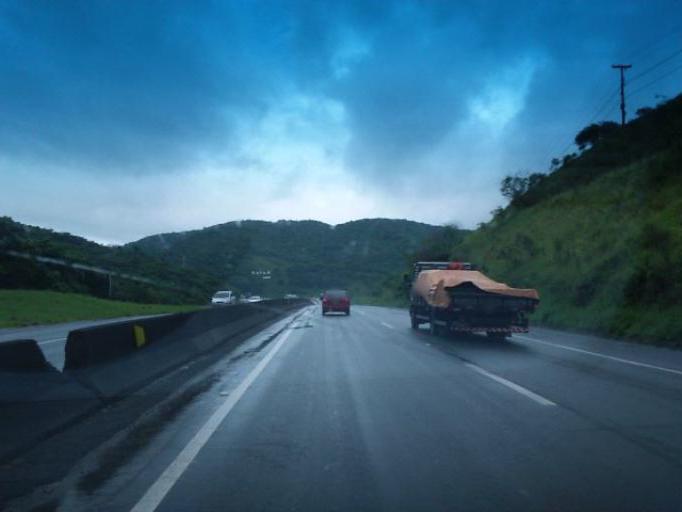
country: BR
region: Santa Catarina
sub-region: Itajai
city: Itajai
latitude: -26.9572
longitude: -48.6799
